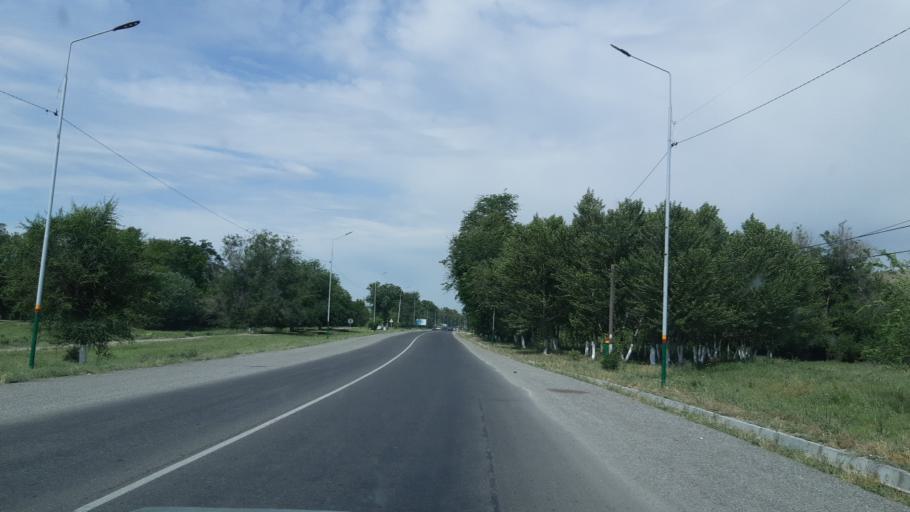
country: KZ
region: Ongtustik Qazaqstan
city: Turar Ryskulov
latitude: 42.5486
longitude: 70.3202
